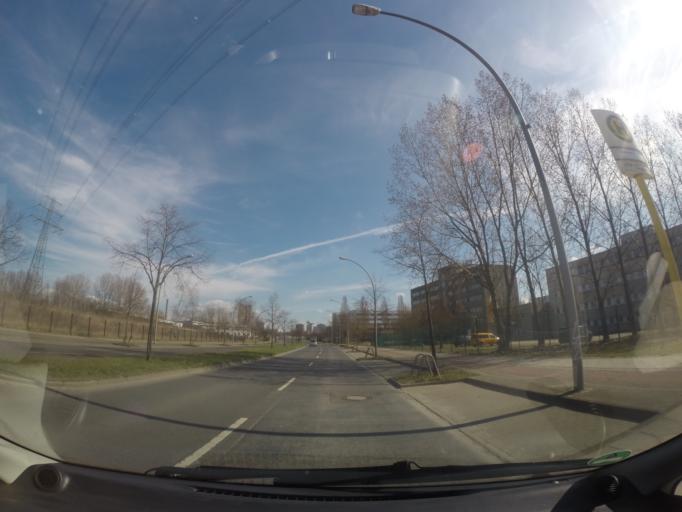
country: DE
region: Berlin
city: Falkenberg
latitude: 52.5540
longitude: 13.5394
